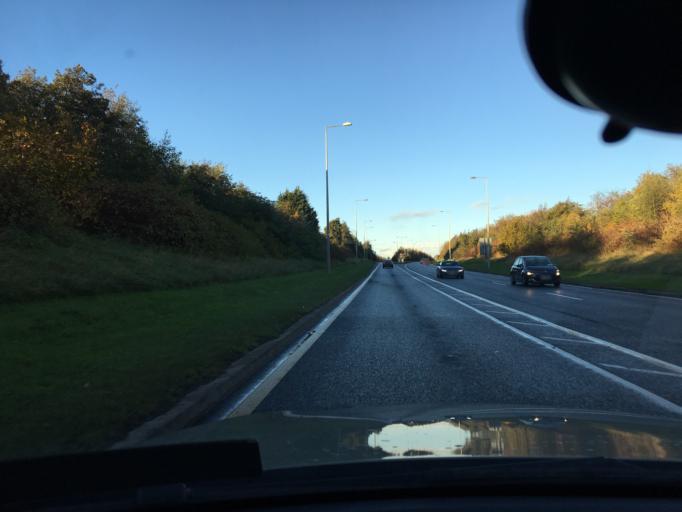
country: IE
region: Leinster
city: Beaumont
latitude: 53.3902
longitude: -6.2420
